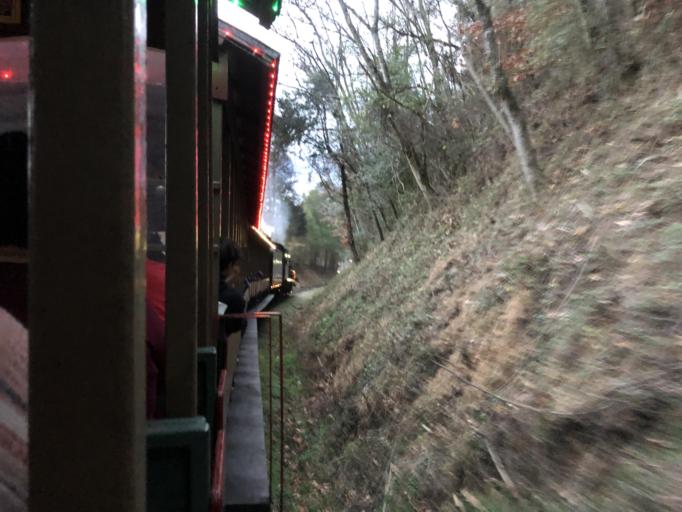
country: US
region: Tennessee
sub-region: Sevier County
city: Pigeon Forge
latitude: 35.7994
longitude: -83.5305
